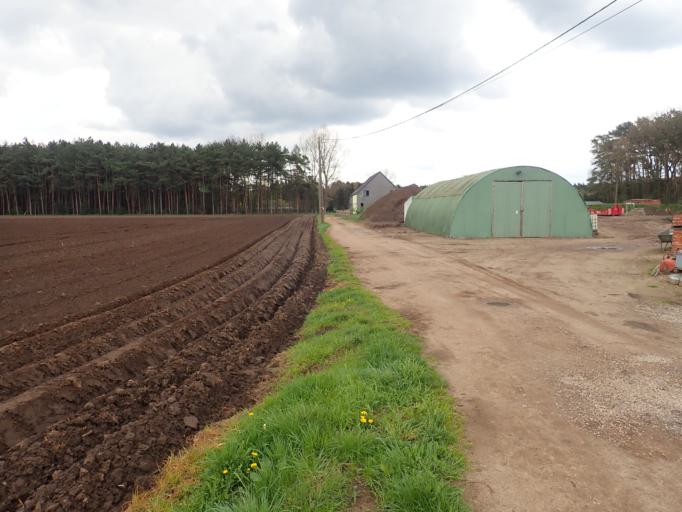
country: BE
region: Flanders
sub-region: Provincie Antwerpen
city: Lille
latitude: 51.2207
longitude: 4.8148
